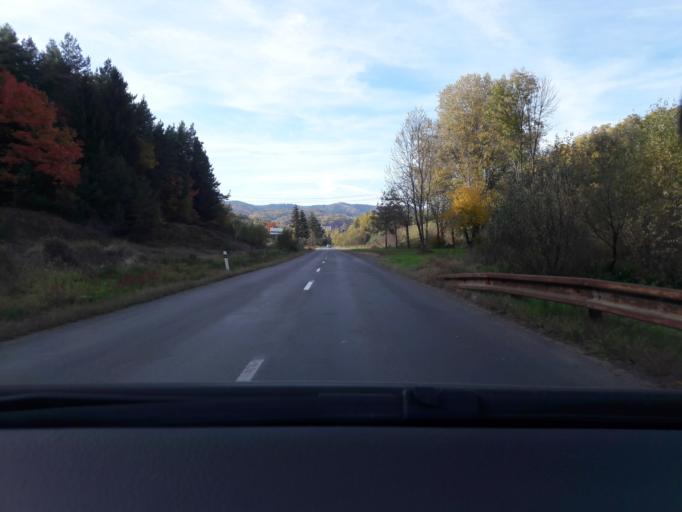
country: SK
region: Banskobystricky
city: Svaety Anton
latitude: 48.4330
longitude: 18.9304
